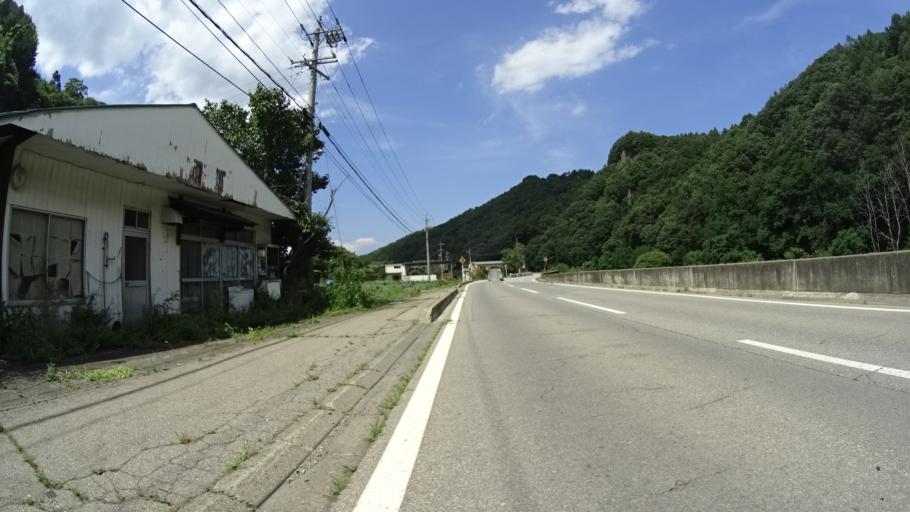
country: JP
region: Nagano
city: Saku
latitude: 36.0698
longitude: 138.4973
